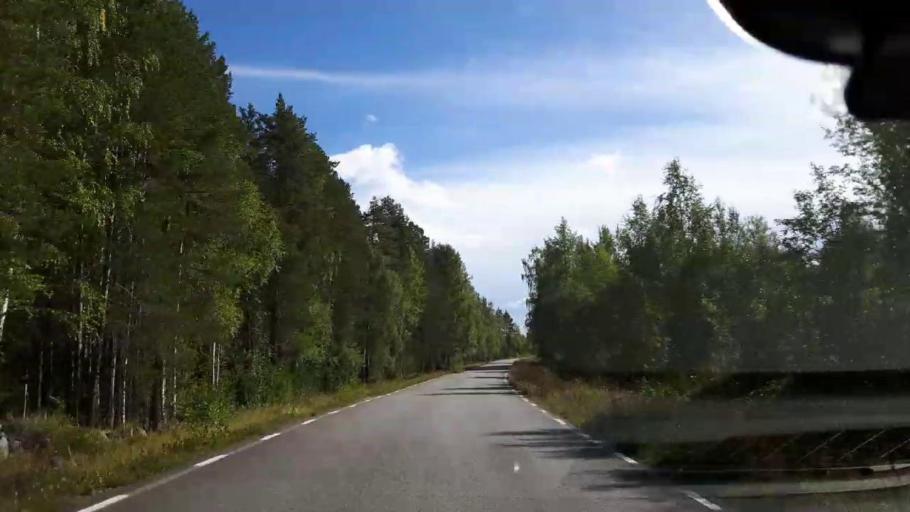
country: SE
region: Jaemtland
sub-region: Braecke Kommun
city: Braecke
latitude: 63.2235
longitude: 15.3047
